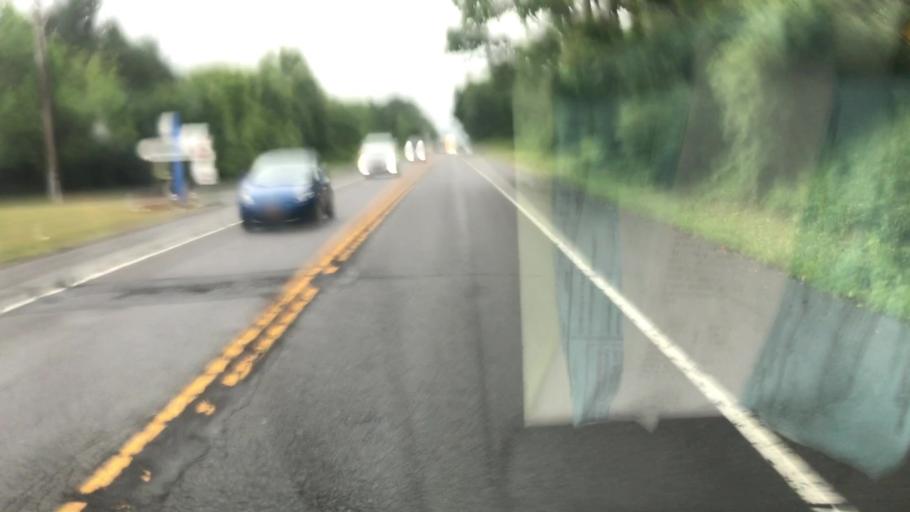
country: US
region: New York
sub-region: Onondaga County
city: Fayetteville
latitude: 43.0192
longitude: -76.0237
